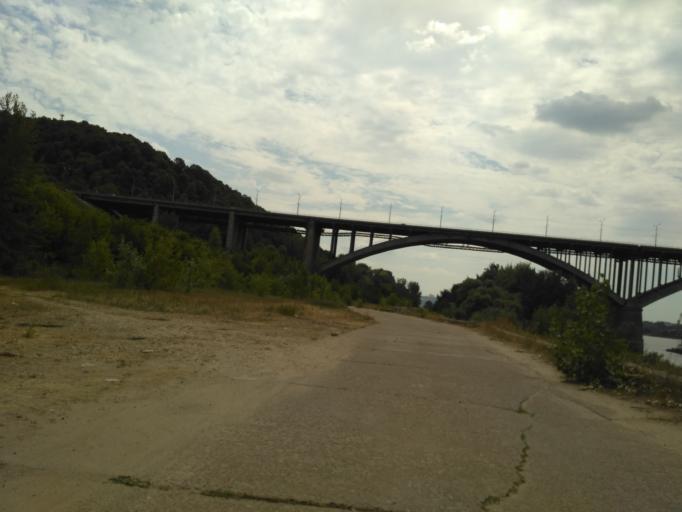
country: RU
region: Nizjnij Novgorod
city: Nizhniy Novgorod
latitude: 56.3012
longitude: 43.9674
